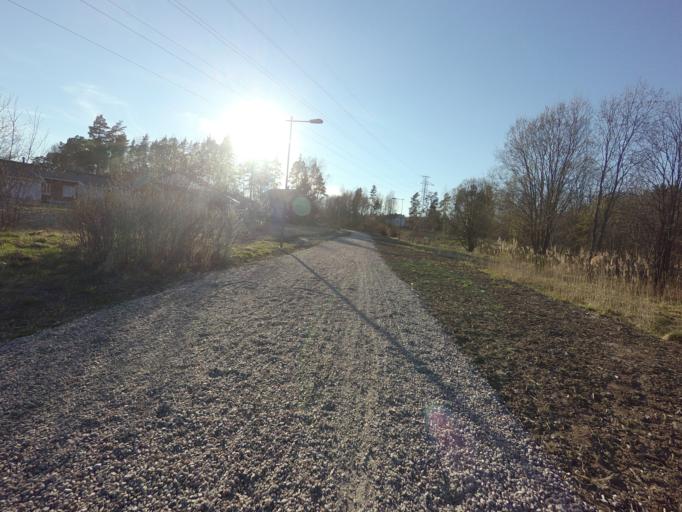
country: FI
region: Uusimaa
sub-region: Helsinki
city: Espoo
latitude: 60.1781
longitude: 24.6889
